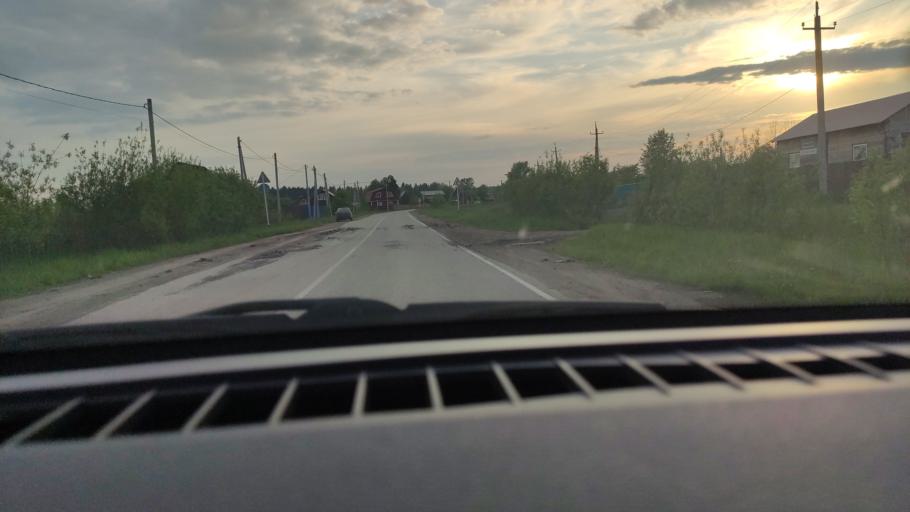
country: RU
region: Perm
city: Overyata
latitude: 58.0777
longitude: 55.9834
